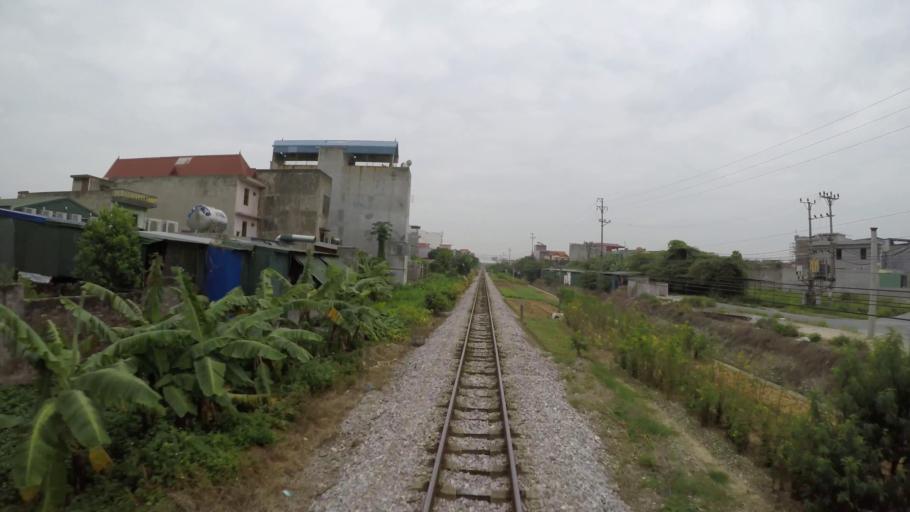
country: VN
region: Hai Phong
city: An Duong
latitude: 20.9160
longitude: 106.5641
